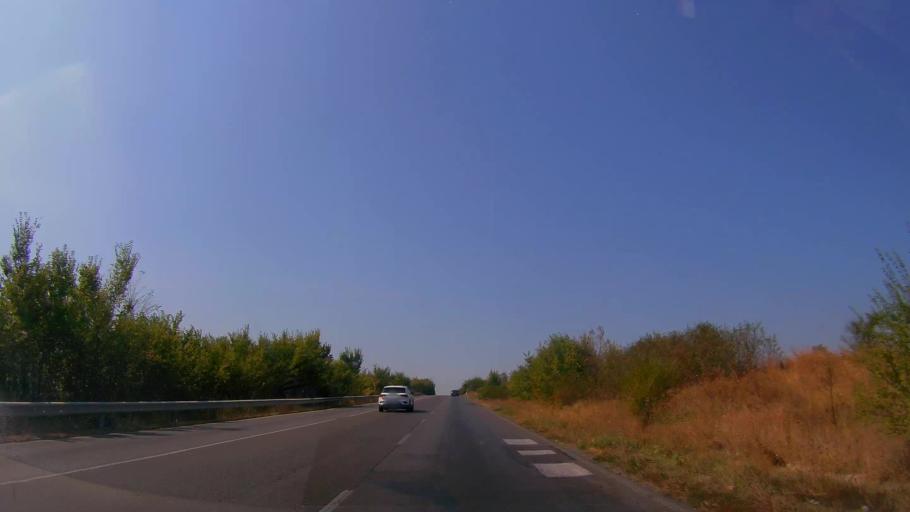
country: BG
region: Ruse
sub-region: Obshtina Vetovo
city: Senovo
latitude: 43.5613
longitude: 26.3672
